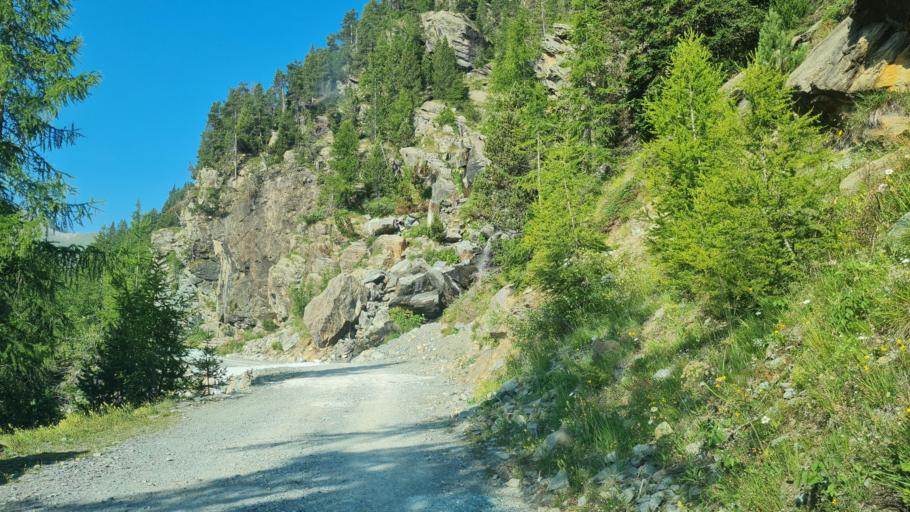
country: IT
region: Aosta Valley
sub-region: Valle d'Aosta
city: Champorcher
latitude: 45.6260
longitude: 7.5944
